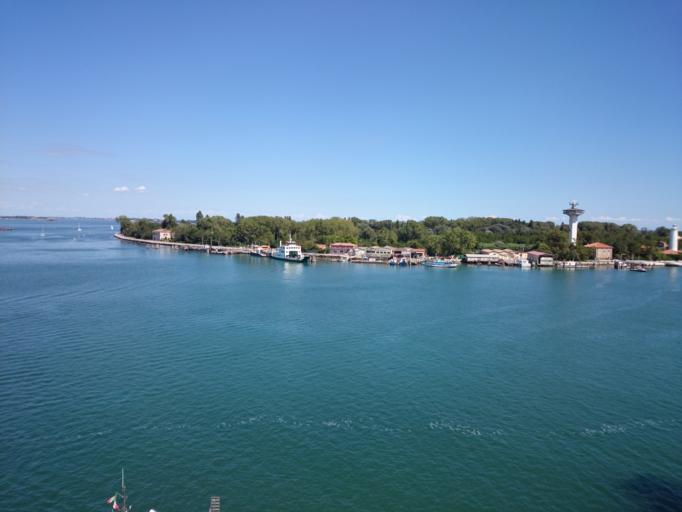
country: IT
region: Veneto
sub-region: Provincia di Venezia
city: San Pietro in Volta
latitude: 45.3390
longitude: 12.3056
